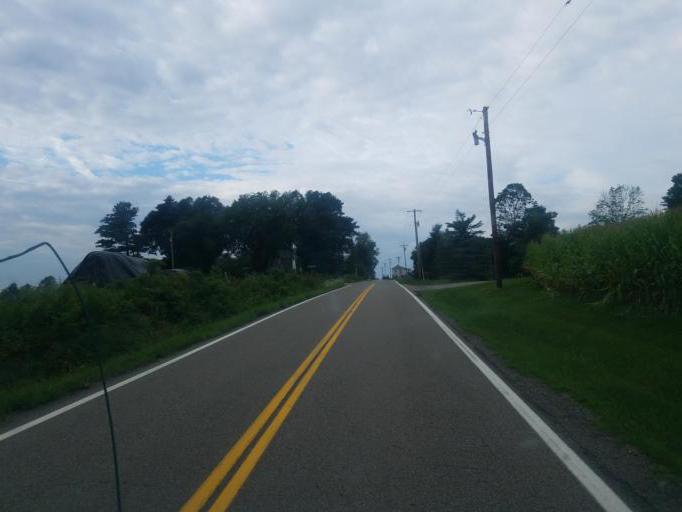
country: US
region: Ohio
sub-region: Knox County
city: Oak Hill
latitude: 40.4156
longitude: -82.1381
